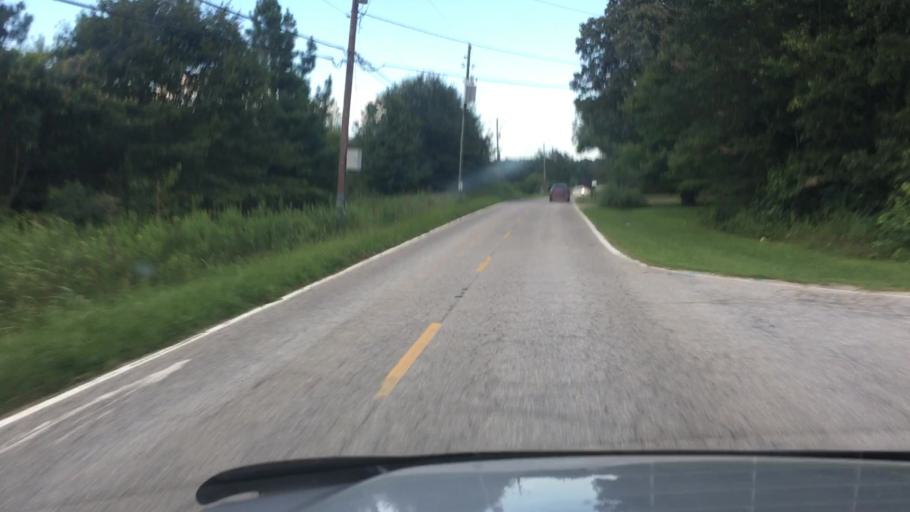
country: US
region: South Carolina
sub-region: Spartanburg County
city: Mayo
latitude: 35.1335
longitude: -81.8326
